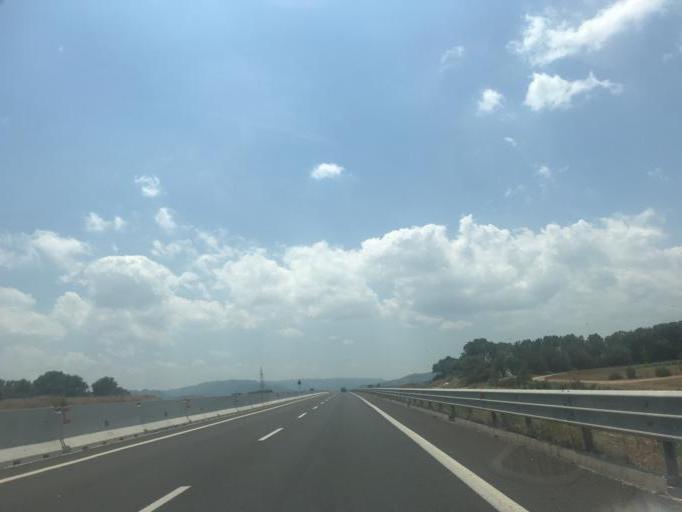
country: IT
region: Sardinia
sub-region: Provincia di Olbia-Tempio
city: Olbia
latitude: 40.8878
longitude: 9.4780
